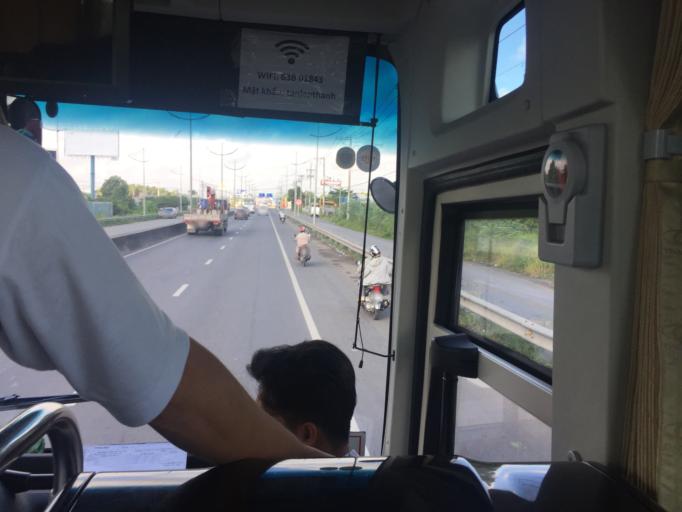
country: VN
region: Ho Chi Minh City
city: Tan Tuc
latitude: 10.6869
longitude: 106.5795
